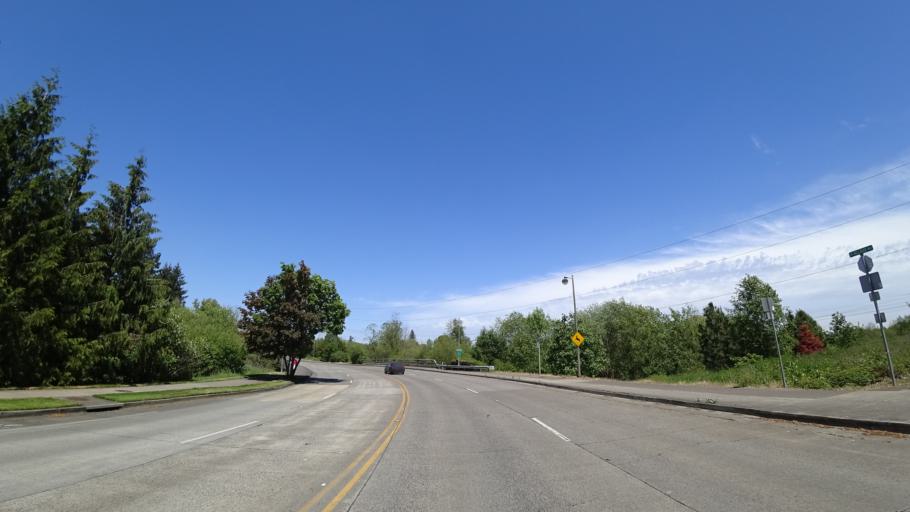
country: US
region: Oregon
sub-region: Washington County
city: Aloha
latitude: 45.4934
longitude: -122.8404
